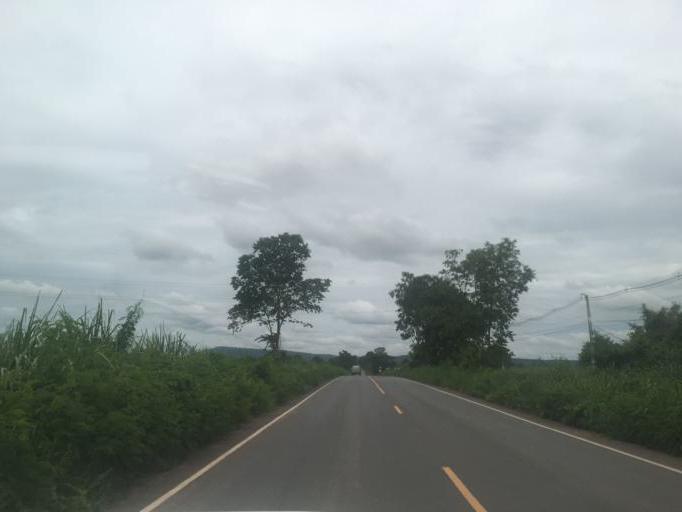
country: TH
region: Changwat Udon Thani
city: Udon Thani
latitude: 17.3067
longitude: 102.7064
